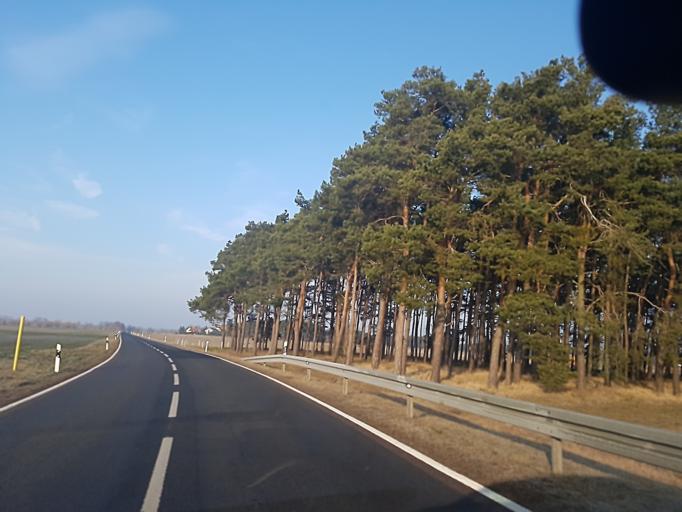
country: DE
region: Brandenburg
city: Golzow
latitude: 52.2540
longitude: 12.6881
